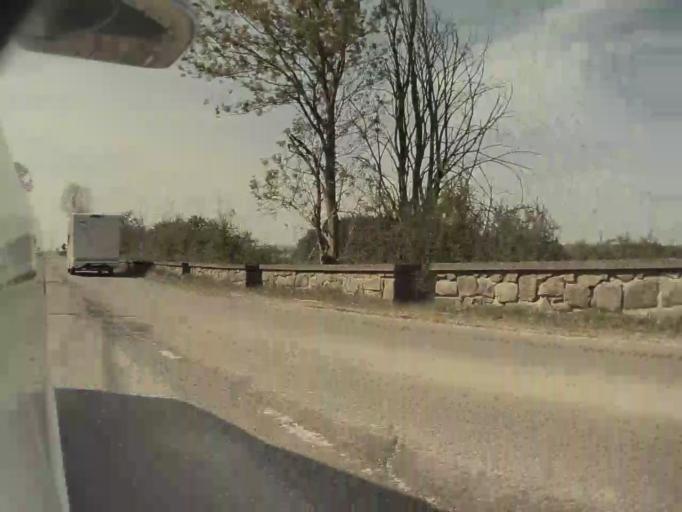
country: BE
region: Wallonia
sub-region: Province de Namur
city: Dinant
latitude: 50.2617
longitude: 4.9662
